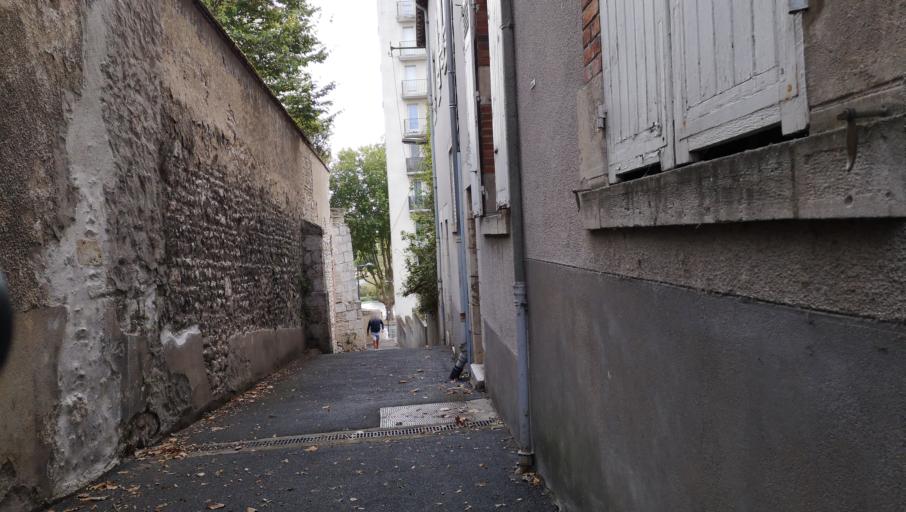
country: FR
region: Centre
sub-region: Departement du Loiret
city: Orleans
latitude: 47.8987
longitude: 1.8912
